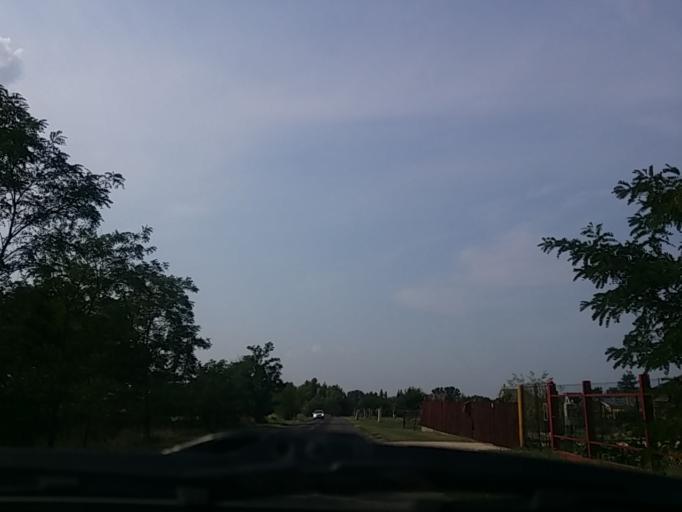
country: HU
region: Komarom-Esztergom
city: Oroszlany
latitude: 47.5023
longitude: 18.3675
